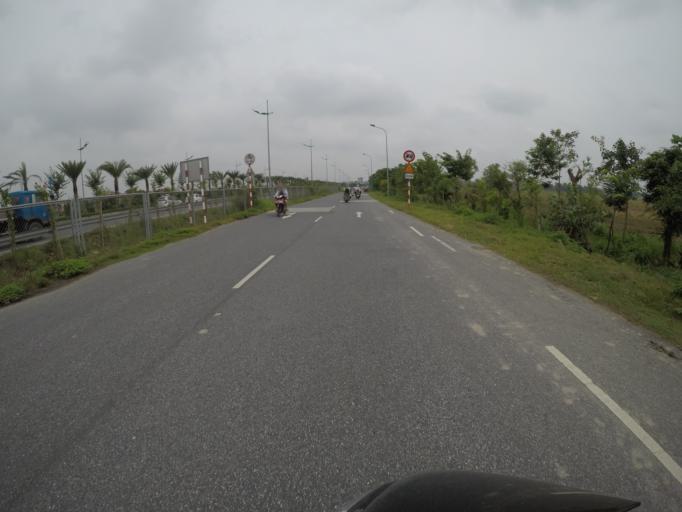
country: VN
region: Ha Noi
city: Dong Anh
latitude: 21.1911
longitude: 105.8333
